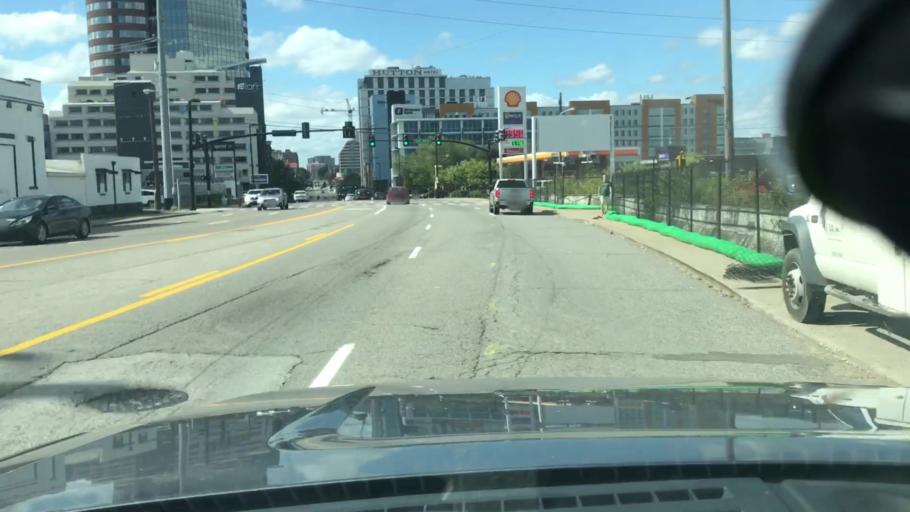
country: US
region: Tennessee
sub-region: Davidson County
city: Nashville
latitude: 36.1540
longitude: -86.7938
